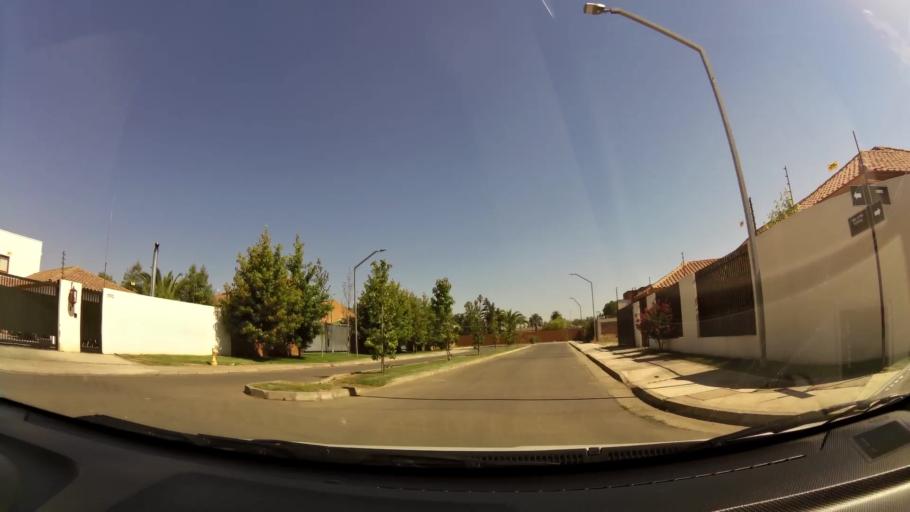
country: CL
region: Maule
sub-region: Provincia de Talca
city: Talca
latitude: -35.4370
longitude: -71.6147
